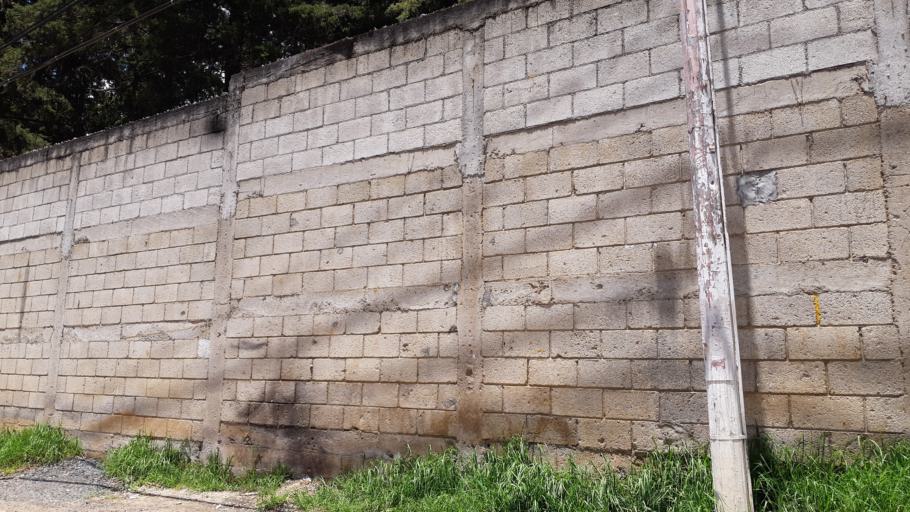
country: GT
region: Chimaltenango
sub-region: Municipio de Chimaltenango
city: Chimaltenango
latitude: 14.6627
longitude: -90.8417
